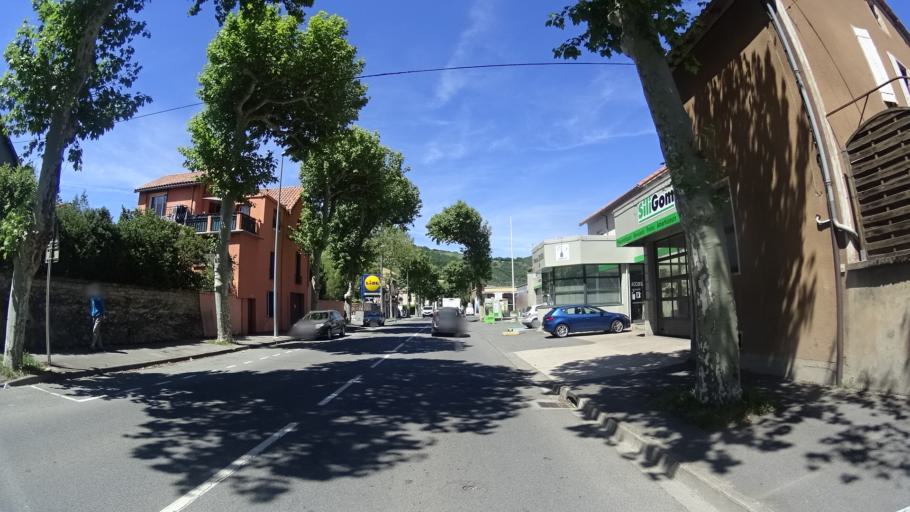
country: FR
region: Midi-Pyrenees
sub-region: Departement de l'Aveyron
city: Millau
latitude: 44.1120
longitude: 3.0823
